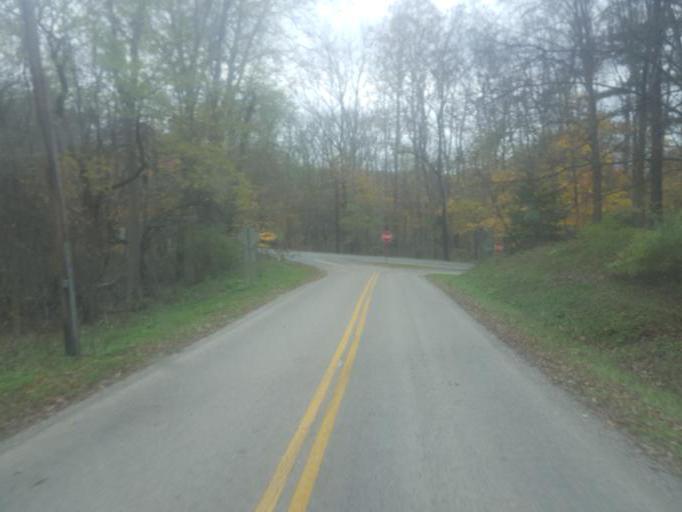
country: US
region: Ohio
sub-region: Richland County
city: Lincoln Heights
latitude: 40.7341
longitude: -82.3623
